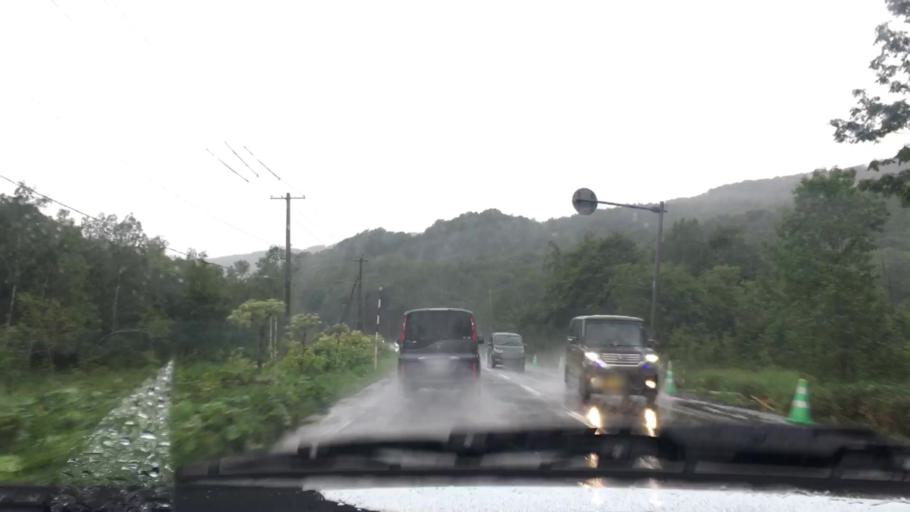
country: JP
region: Hokkaido
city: Otaru
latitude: 42.8489
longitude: 141.0277
